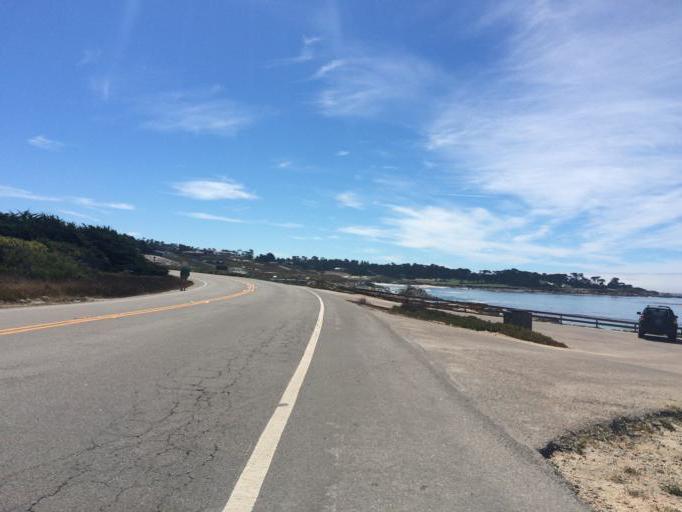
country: US
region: California
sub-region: Monterey County
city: Del Monte Forest
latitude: 36.5882
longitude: -121.9636
